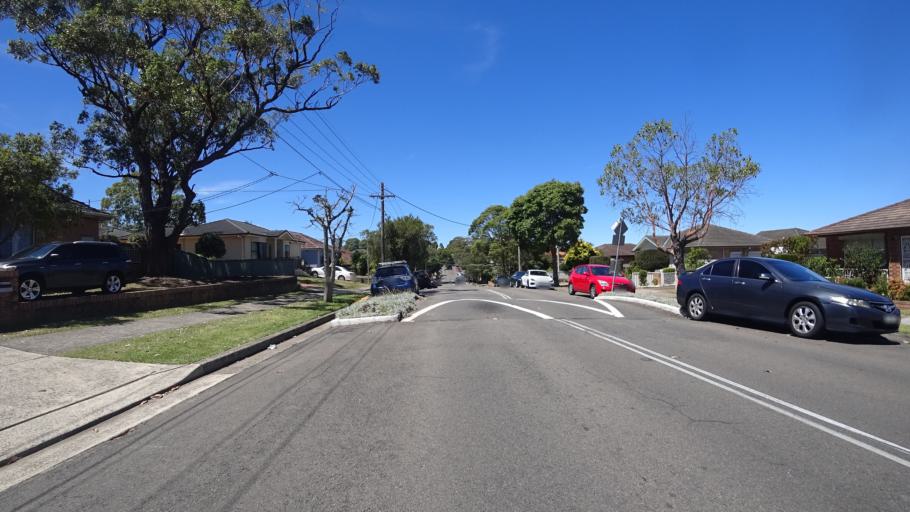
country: AU
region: New South Wales
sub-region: Rockdale
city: Bexley
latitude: -33.9570
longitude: 151.1234
